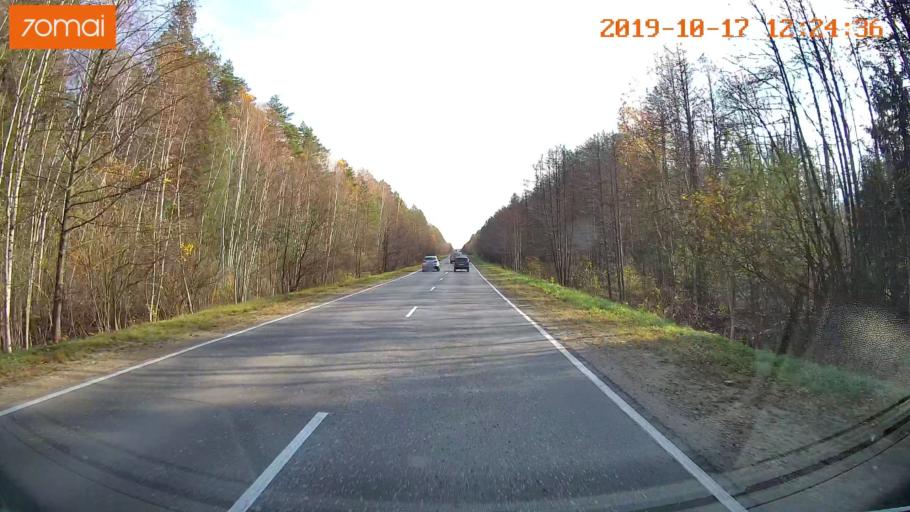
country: RU
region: Rjazan
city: Gus'-Zheleznyy
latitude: 55.0342
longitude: 41.2181
